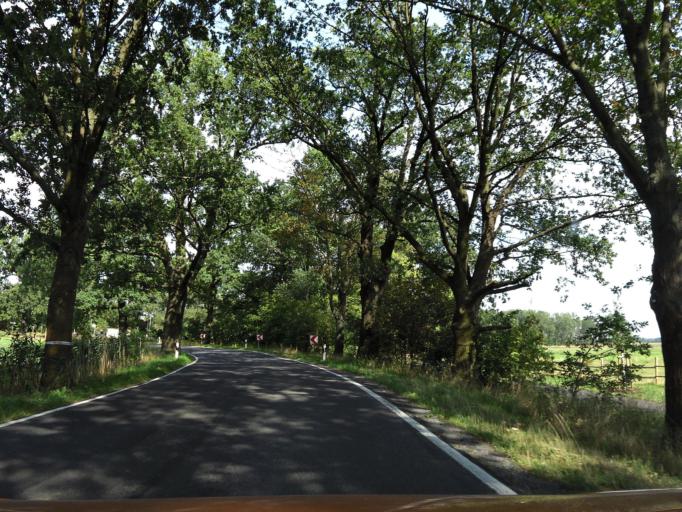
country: DE
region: Berlin
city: Wannsee
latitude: 52.3229
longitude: 13.1330
